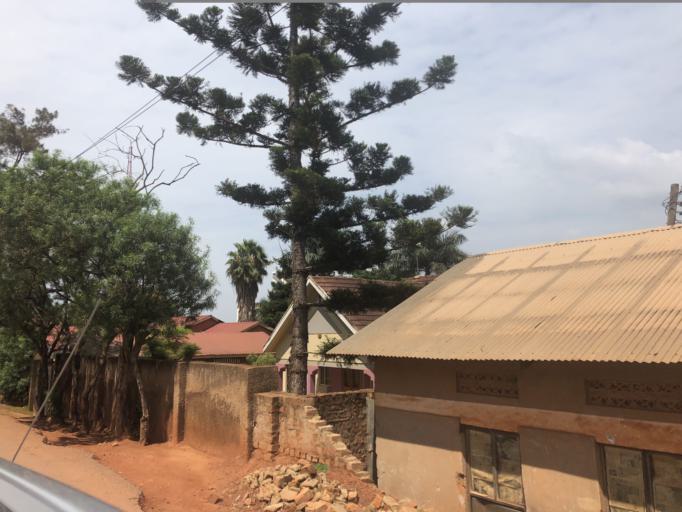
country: UG
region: Central Region
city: Kampala Central Division
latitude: 0.3555
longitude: 32.5979
